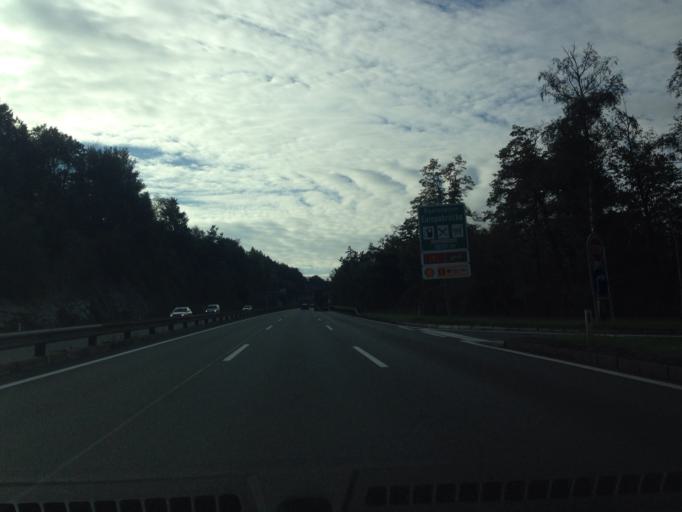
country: AT
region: Tyrol
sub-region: Politischer Bezirk Innsbruck Land
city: Patsch
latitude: 47.2130
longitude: 11.3995
